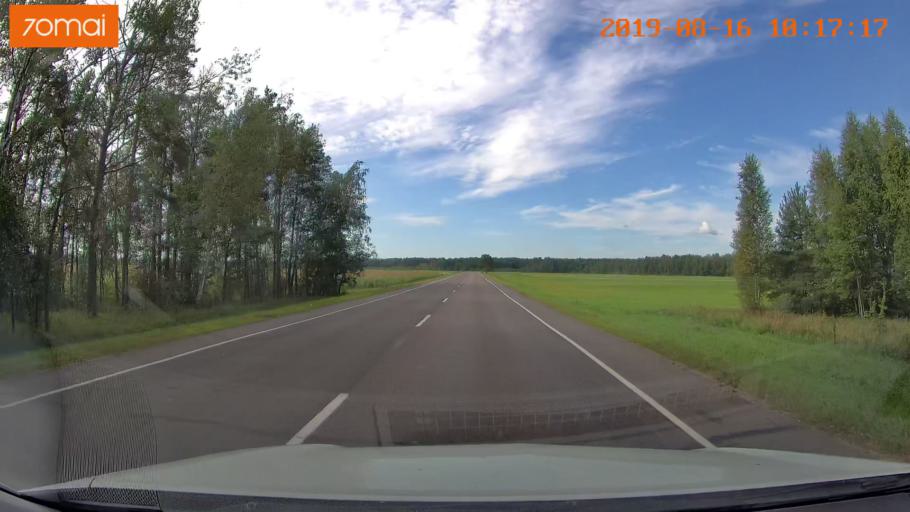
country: BY
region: Mogilev
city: Asipovichy
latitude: 53.3128
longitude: 28.7131
